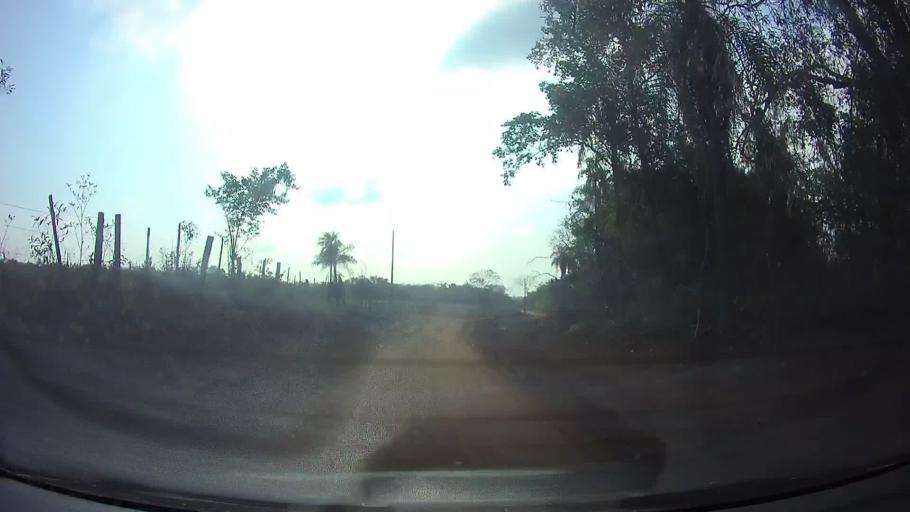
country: PY
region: Cordillera
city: Arroyos y Esteros
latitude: -25.0199
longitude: -57.1937
